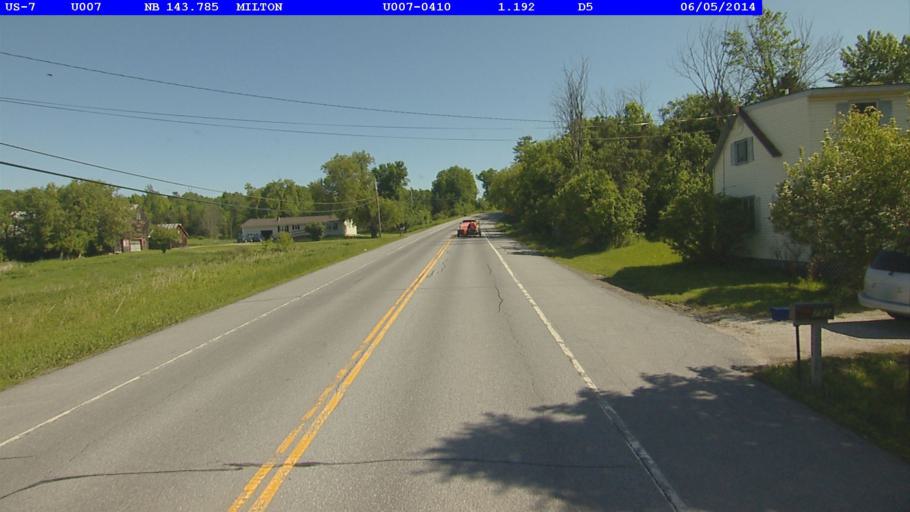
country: US
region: Vermont
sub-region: Chittenden County
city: Milton
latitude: 44.6111
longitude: -73.1546
